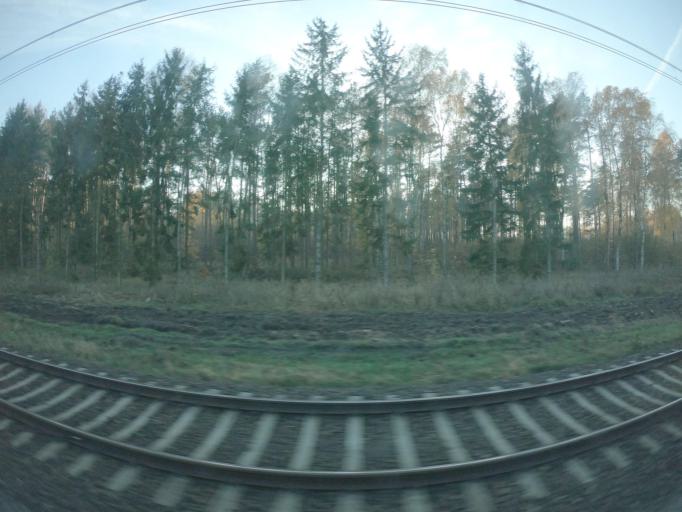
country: PL
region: Lubusz
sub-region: Powiat slubicki
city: Rzepin
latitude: 52.2708
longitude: 14.9252
